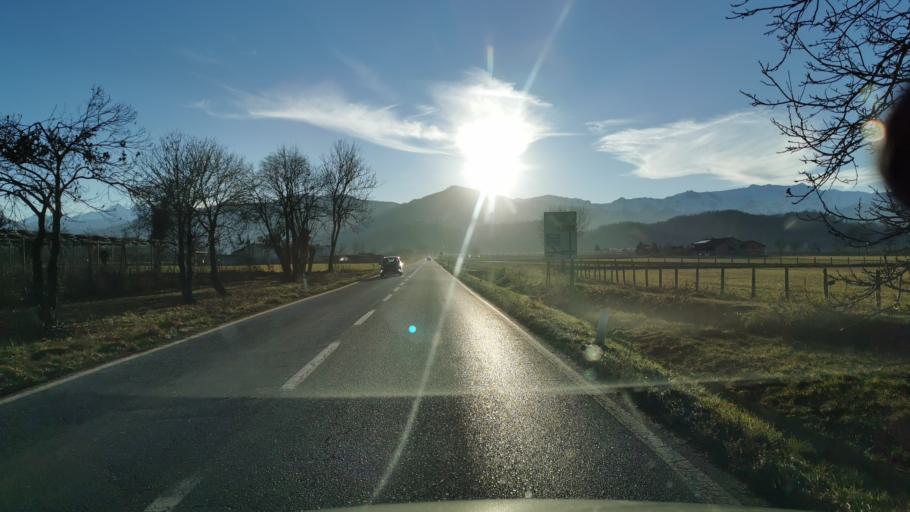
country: IT
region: Piedmont
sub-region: Provincia di Cuneo
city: Caraglio
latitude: 44.4348
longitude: 7.4445
